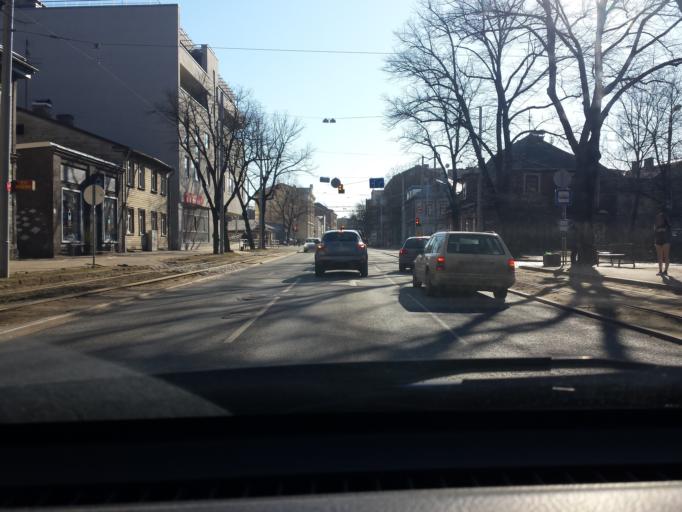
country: LV
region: Riga
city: Riga
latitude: 56.9662
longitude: 24.1338
